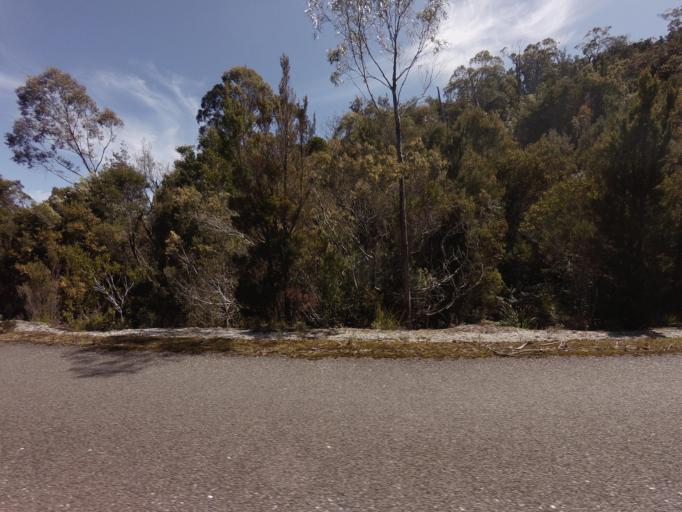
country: AU
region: Tasmania
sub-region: Huon Valley
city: Geeveston
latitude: -42.8585
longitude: 146.2300
